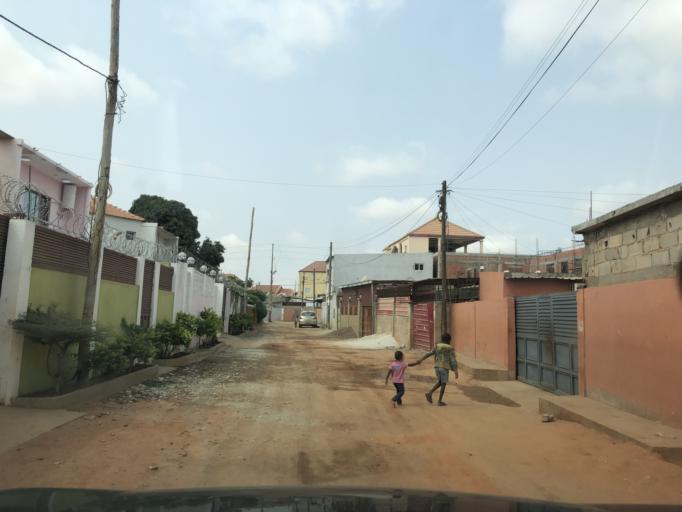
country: AO
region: Luanda
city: Luanda
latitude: -8.9172
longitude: 13.1715
